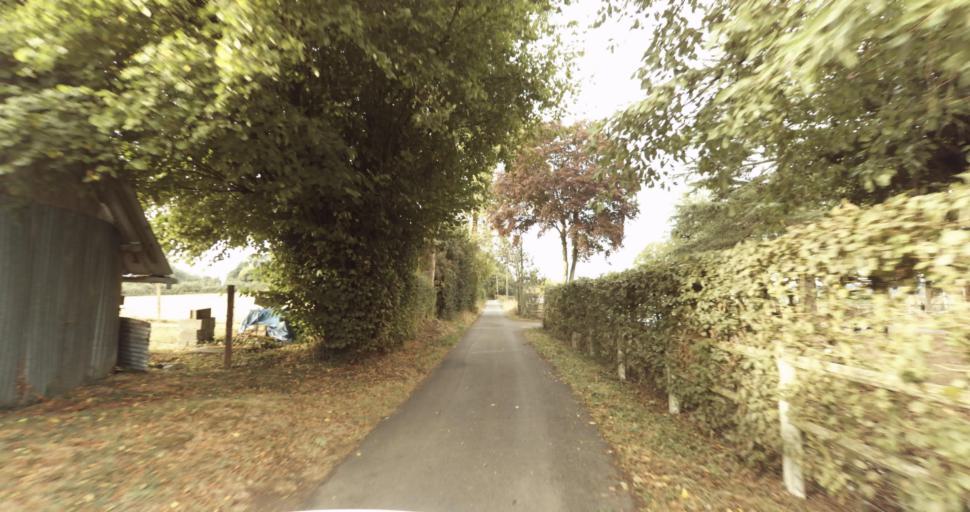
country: FR
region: Lower Normandy
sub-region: Departement du Calvados
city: Livarot
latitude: 48.9227
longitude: 0.0995
